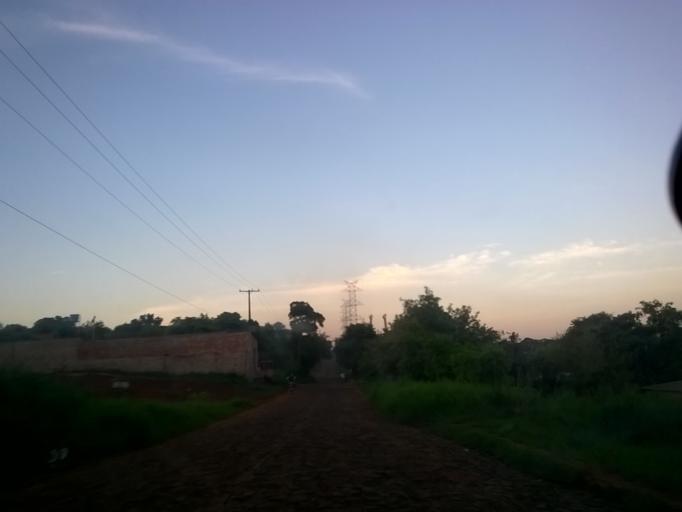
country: PY
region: Alto Parana
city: Ciudad del Este
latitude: -25.4820
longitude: -54.6447
